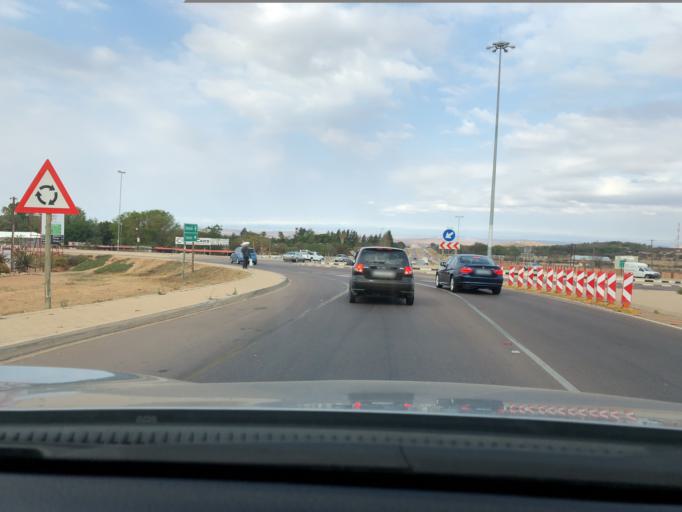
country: ZA
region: Limpopo
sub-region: Capricorn District Municipality
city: Polokwane
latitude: -23.8986
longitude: 29.5222
